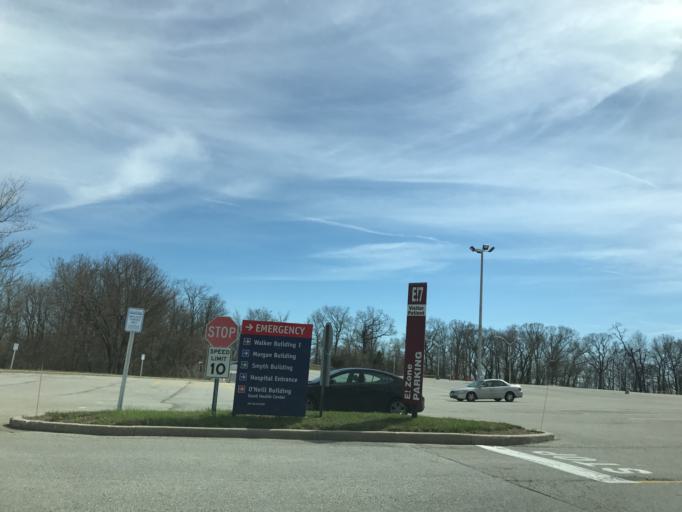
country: US
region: Maryland
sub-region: Baltimore County
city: Towson
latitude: 39.3578
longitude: -76.5850
